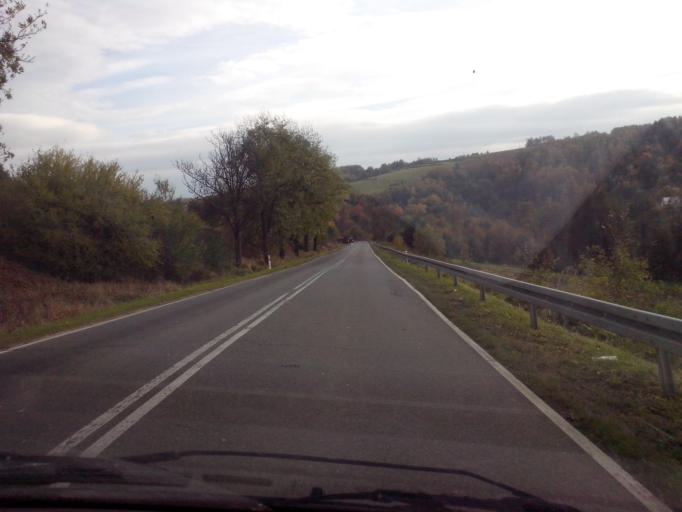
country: PL
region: Subcarpathian Voivodeship
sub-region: Powiat ropczycko-sedziszowski
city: Wielopole Skrzynskie
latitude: 49.9112
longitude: 21.6188
